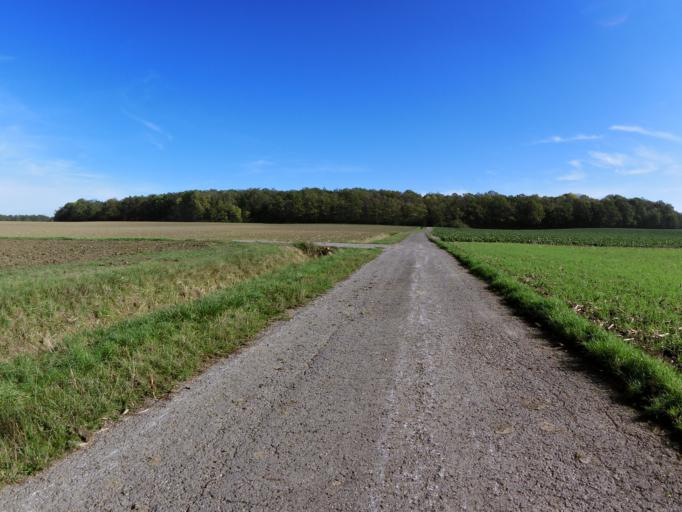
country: DE
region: Bavaria
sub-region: Regierungsbezirk Unterfranken
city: Frickenhausen
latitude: 49.7102
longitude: 10.0899
